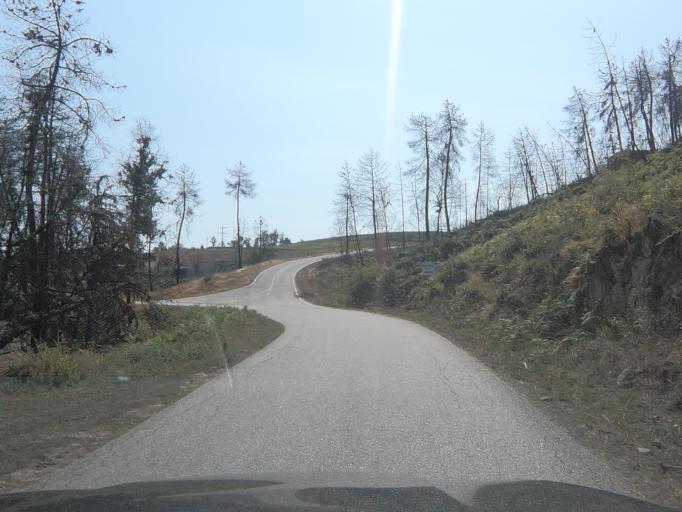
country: PT
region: Vila Real
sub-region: Sabrosa
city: Sabrosa
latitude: 41.3413
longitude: -7.5950
